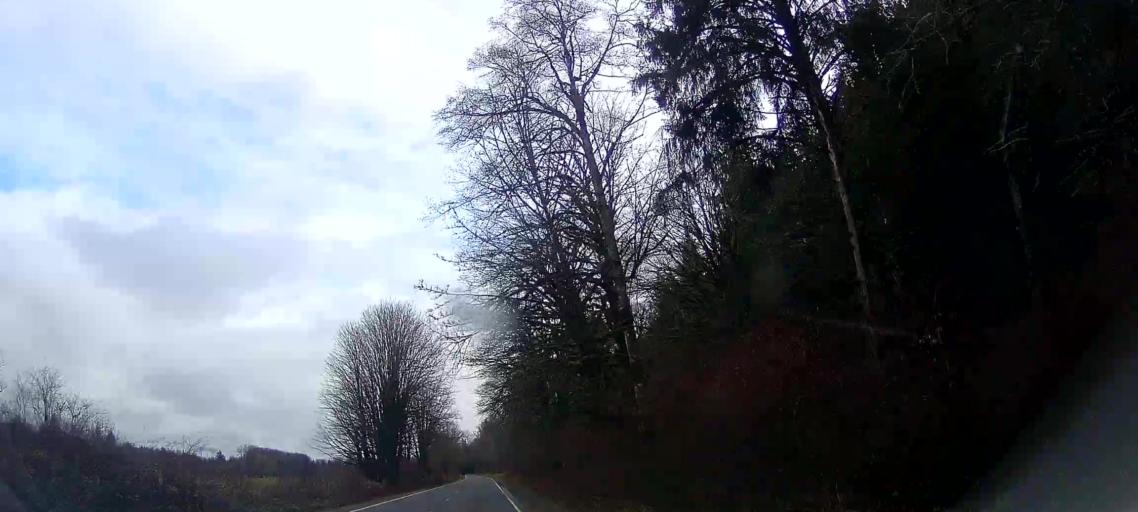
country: US
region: Washington
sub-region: Skagit County
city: Sedro-Woolley
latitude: 48.5149
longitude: -121.9527
